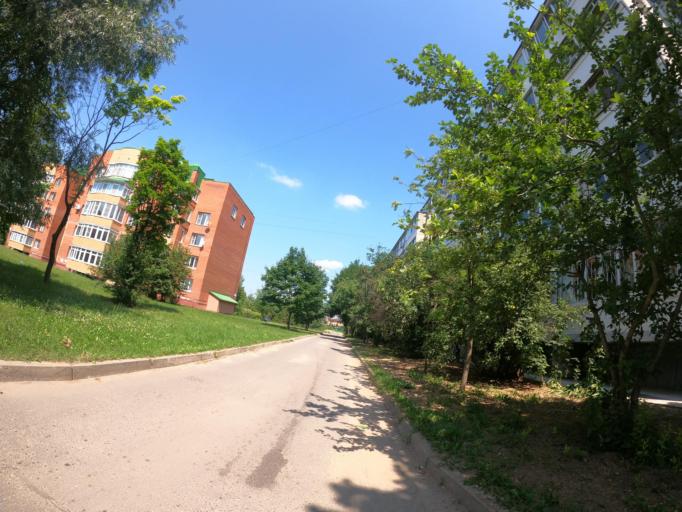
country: RU
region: Kaluga
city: Obninsk
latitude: 55.1213
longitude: 36.5984
